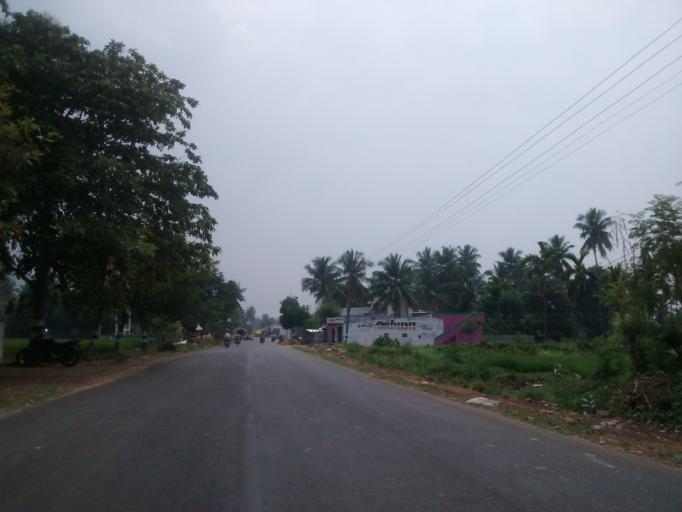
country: IN
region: Tamil Nadu
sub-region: Krishnagiri
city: Kaverippattanam
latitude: 12.4649
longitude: 78.2078
